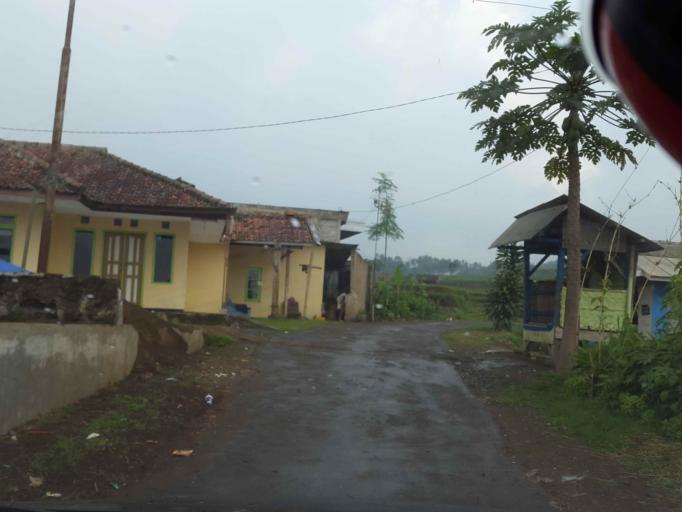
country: ID
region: West Java
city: Padalarang
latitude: -6.8309
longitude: 107.5087
